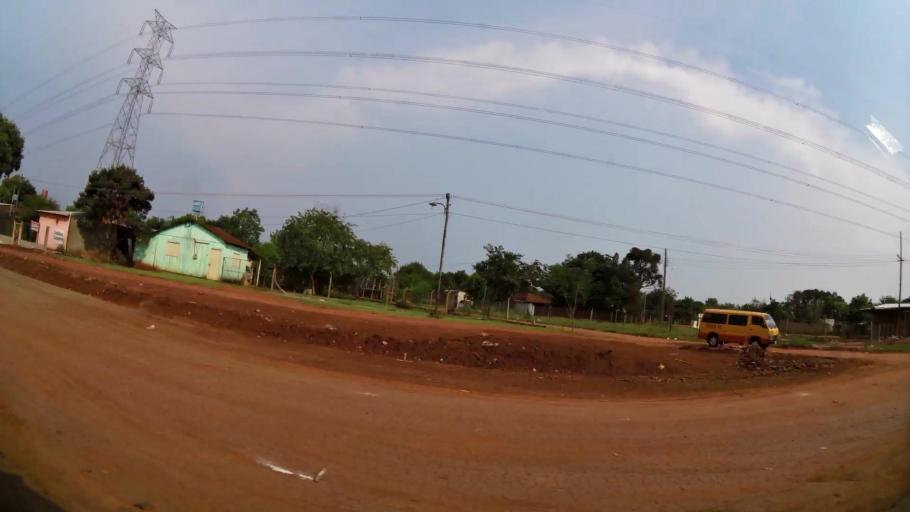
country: PY
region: Alto Parana
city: Ciudad del Este
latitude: -25.4736
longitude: -54.6486
